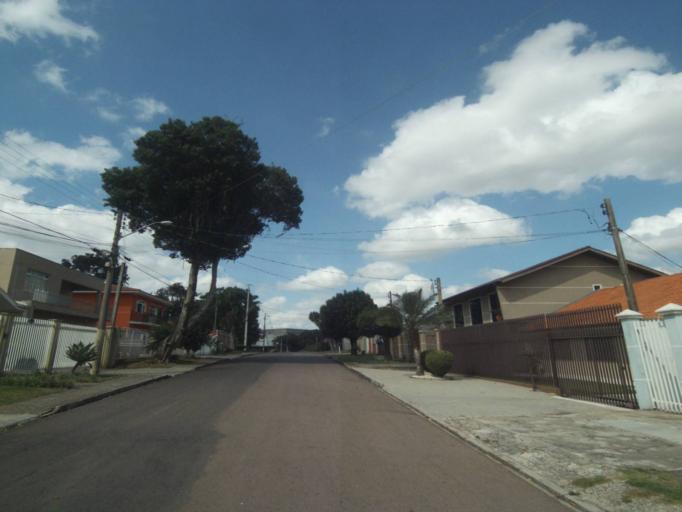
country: BR
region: Parana
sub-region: Curitiba
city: Curitiba
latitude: -25.5003
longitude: -49.3142
